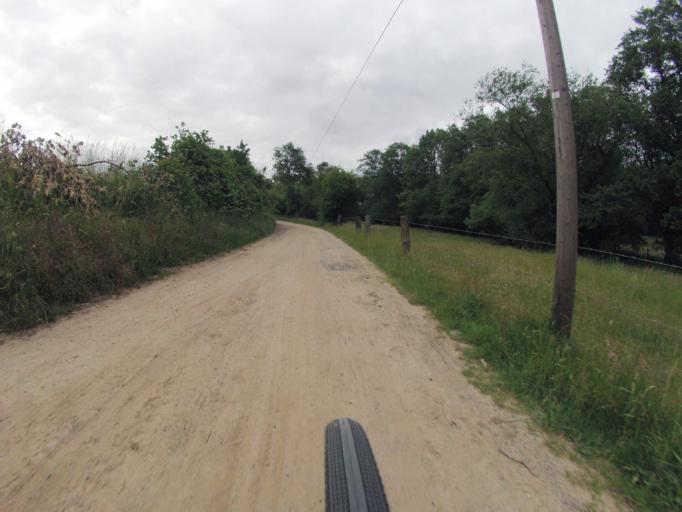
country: DE
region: North Rhine-Westphalia
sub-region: Regierungsbezirk Munster
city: Saerbeck
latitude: 52.1642
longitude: 7.5910
